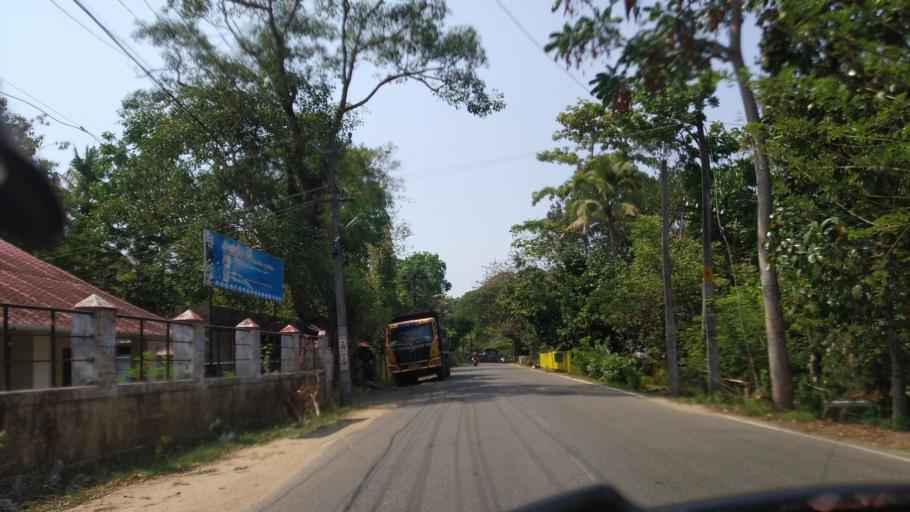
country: IN
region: Kerala
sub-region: Thrissur District
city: Kodungallur
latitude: 10.1991
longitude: 76.1692
